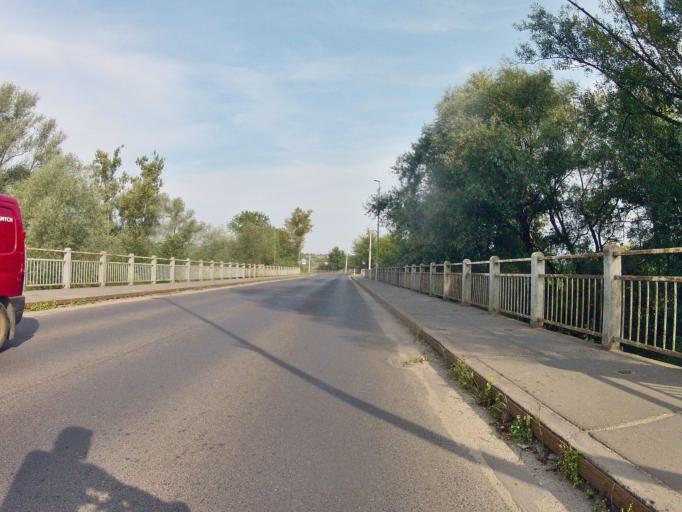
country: PL
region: Subcarpathian Voivodeship
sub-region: Powiat jasielski
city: Jaslo
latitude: 49.7511
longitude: 21.4590
